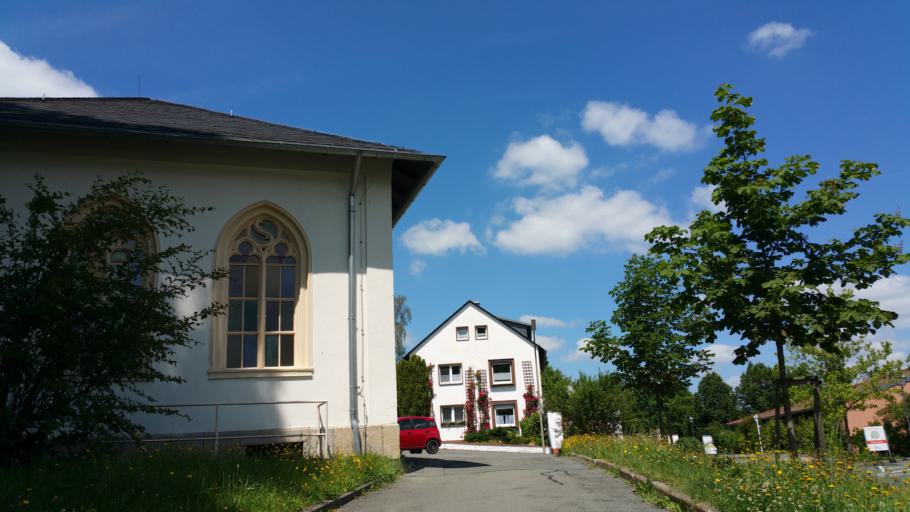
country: DE
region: Bavaria
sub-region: Upper Franconia
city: Schwarzenbach an der Saale
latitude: 50.2253
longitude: 11.9328
